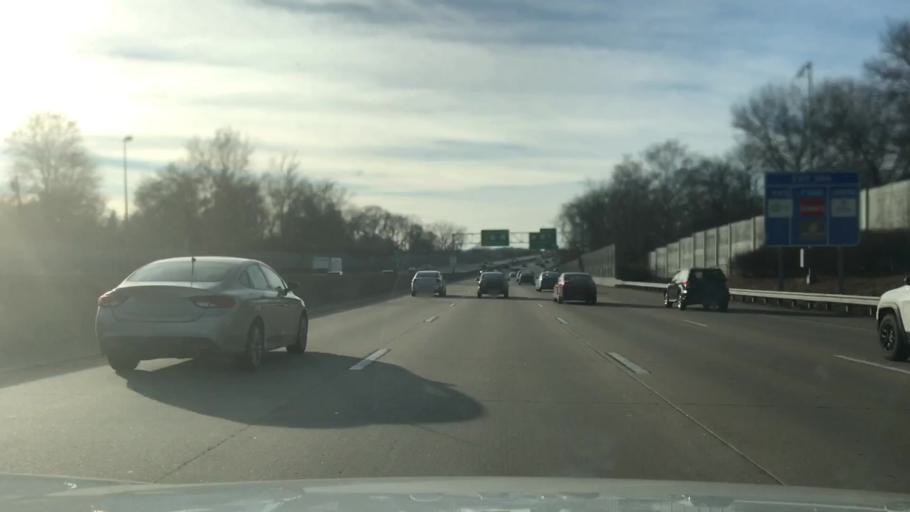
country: US
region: Missouri
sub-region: Saint Louis County
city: Frontenac
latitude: 38.6361
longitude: -90.3983
